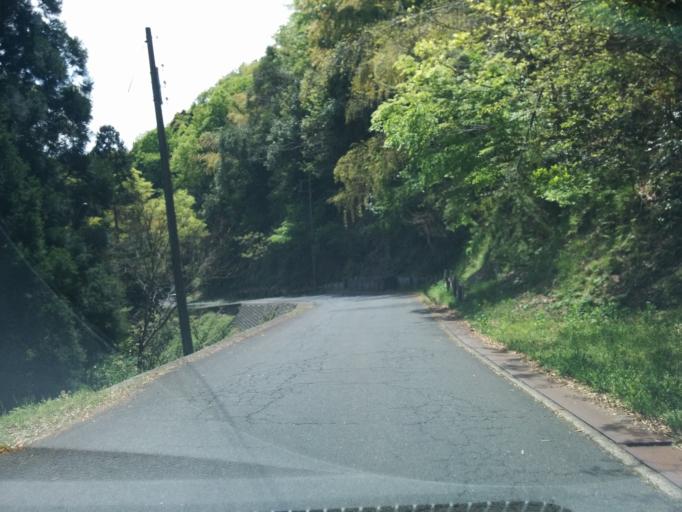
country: JP
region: Kyoto
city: Miyazu
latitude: 35.5923
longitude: 135.1795
